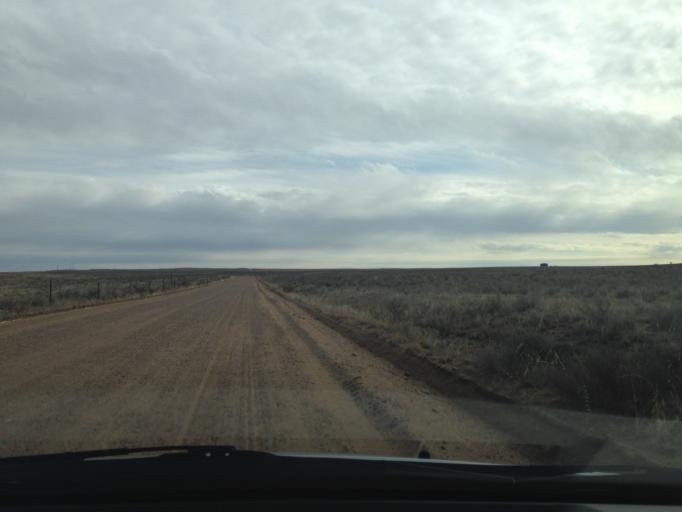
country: US
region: Colorado
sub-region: Weld County
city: Keenesburg
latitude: 40.2811
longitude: -104.2068
